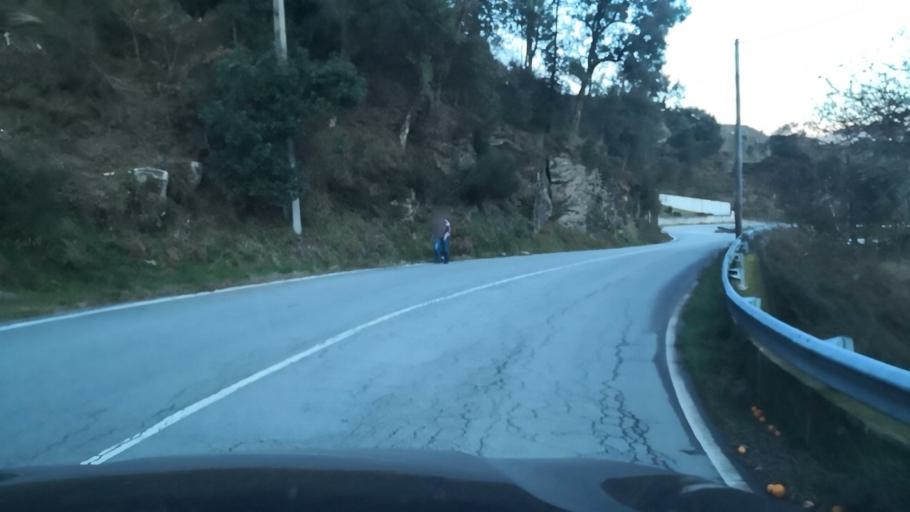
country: PT
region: Vila Real
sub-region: Mondim de Basto
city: Mondim de Basto
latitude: 41.4620
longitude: -7.9614
